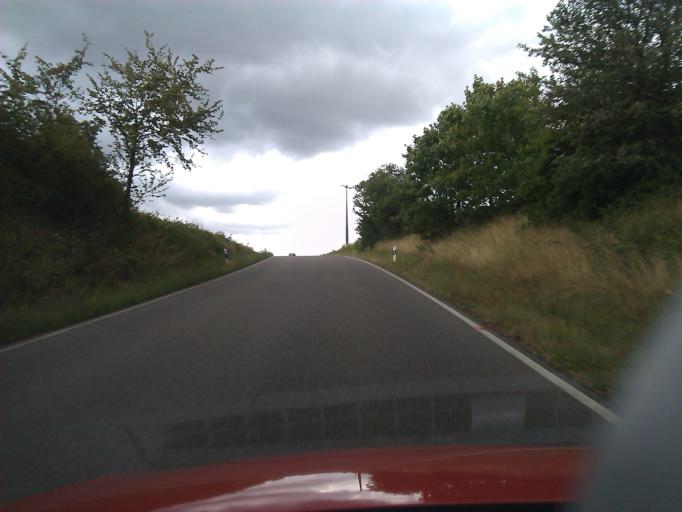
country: DE
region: Baden-Wuerttemberg
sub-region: Regierungsbezirk Stuttgart
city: Pfaffenhofen
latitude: 49.0887
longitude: 8.9844
